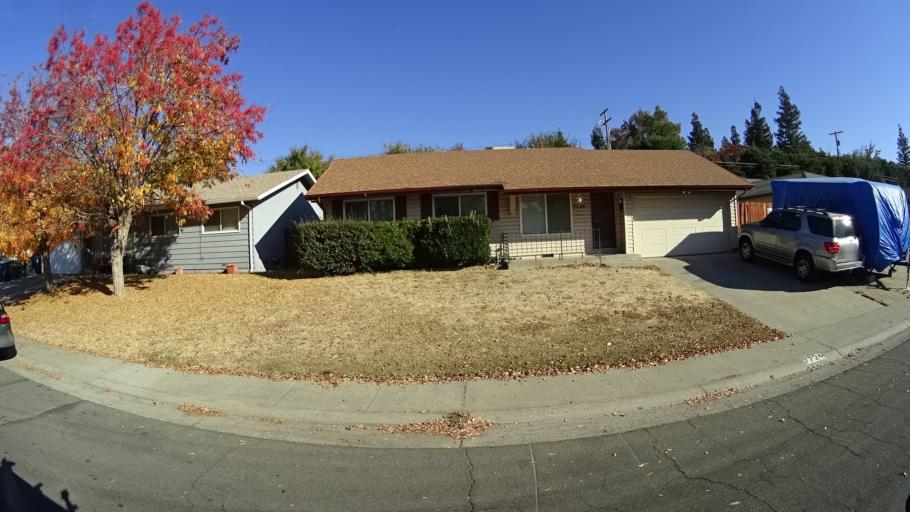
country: US
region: California
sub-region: Sacramento County
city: Antelope
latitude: 38.7061
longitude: -121.3185
